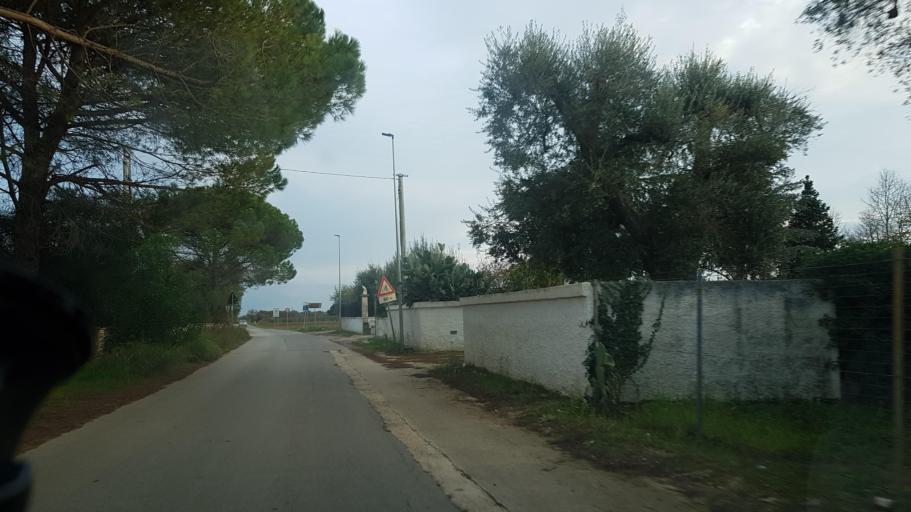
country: IT
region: Apulia
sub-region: Provincia di Brindisi
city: Latiano
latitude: 40.5437
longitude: 17.7351
